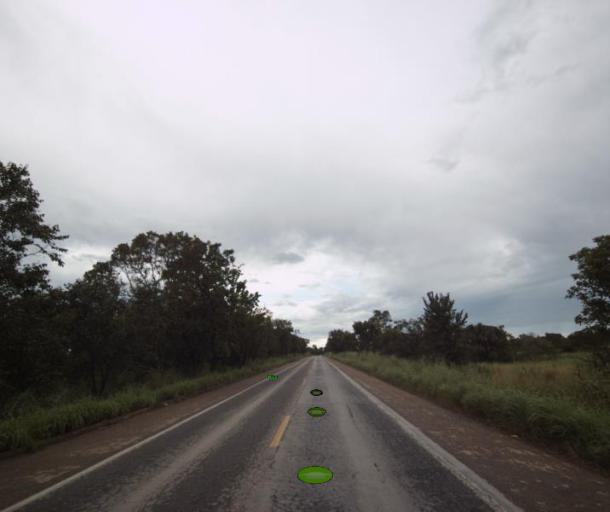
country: BR
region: Goias
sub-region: Porangatu
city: Porangatu
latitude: -13.6750
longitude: -49.0262
